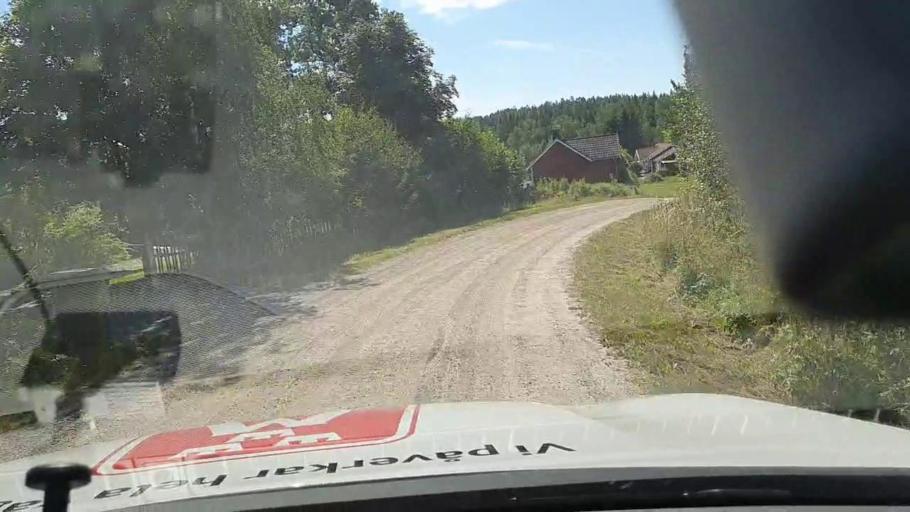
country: SE
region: Soedermanland
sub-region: Strangnas Kommun
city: Akers Styckebruk
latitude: 59.2151
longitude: 16.9104
